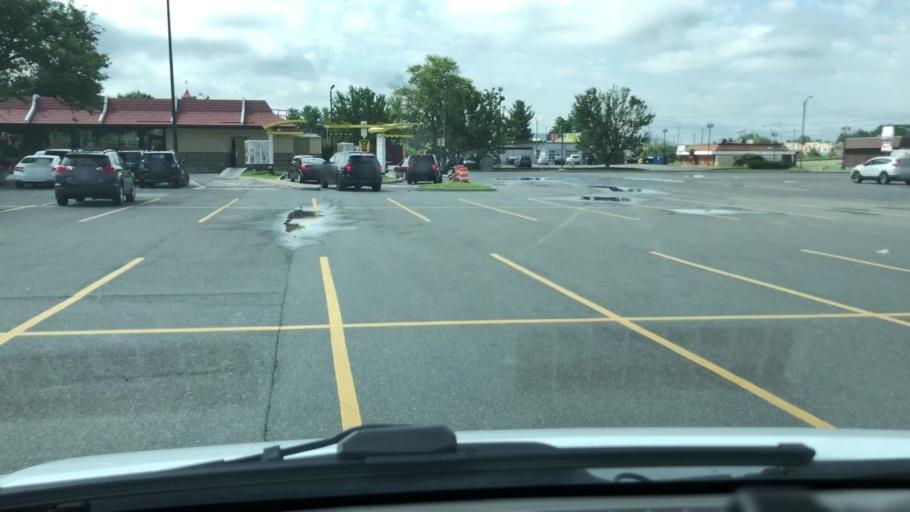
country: US
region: Massachusetts
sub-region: Berkshire County
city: Dalton
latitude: 42.4692
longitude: -73.2043
